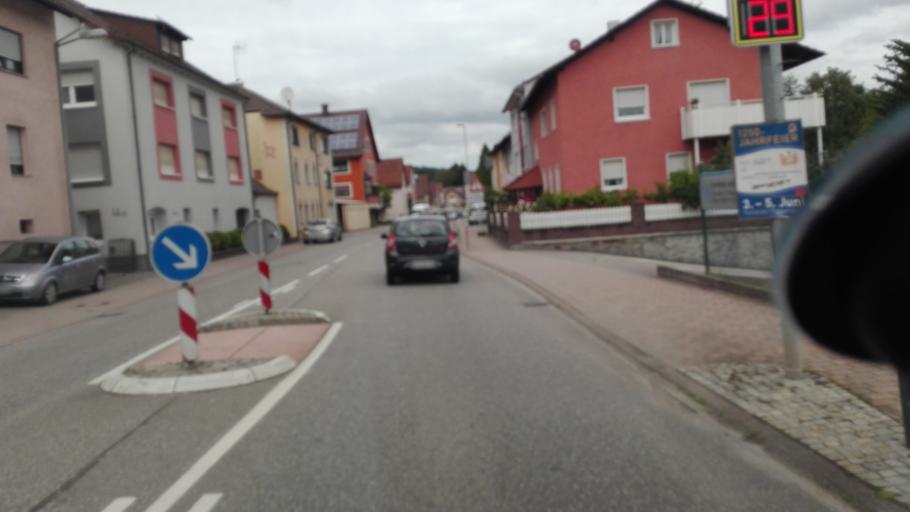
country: DE
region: Baden-Wuerttemberg
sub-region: Karlsruhe Region
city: Konigsbach-Stein
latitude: 48.9631
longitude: 8.5560
